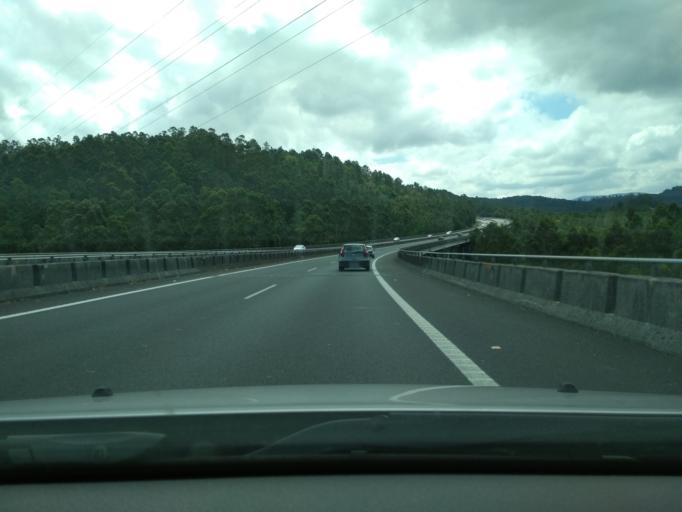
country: ES
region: Galicia
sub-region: Provincia de Pontevedra
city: Portas
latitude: 42.5891
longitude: -8.6760
